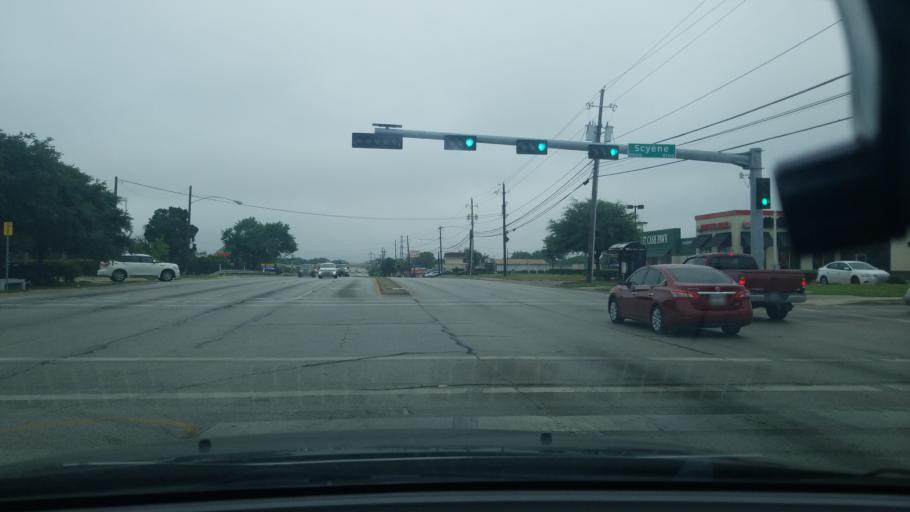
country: US
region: Texas
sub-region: Dallas County
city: Balch Springs
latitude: 32.7632
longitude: -96.6826
